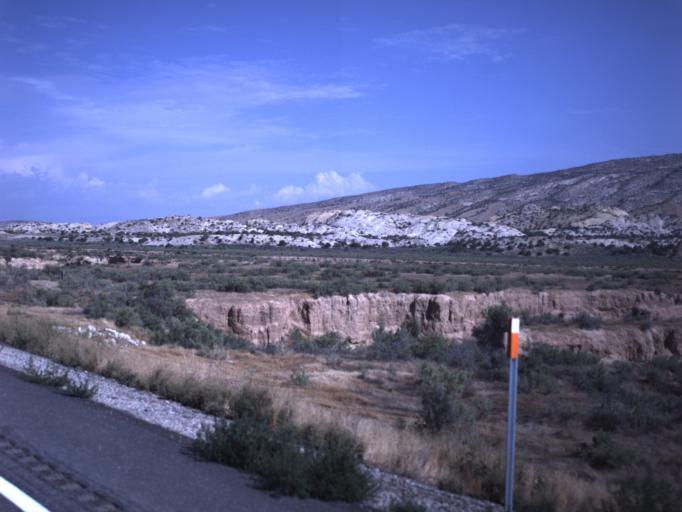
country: US
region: Utah
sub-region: Uintah County
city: Naples
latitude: 40.3142
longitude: -109.2274
